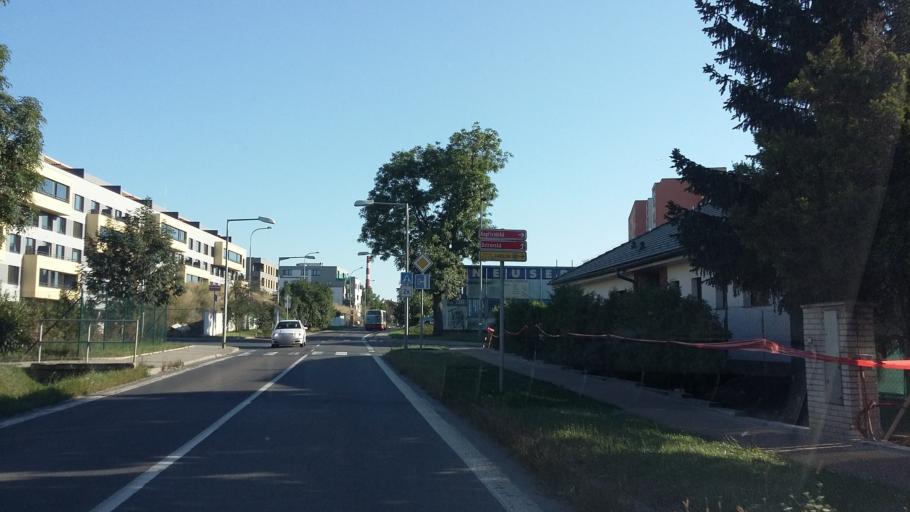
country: CZ
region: Praha
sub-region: Praha 18
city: Letnany
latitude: 50.1402
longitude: 14.5172
